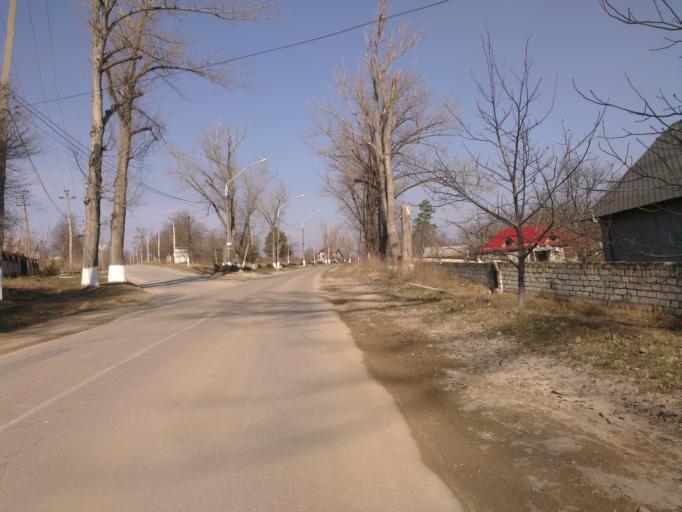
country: MD
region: Chisinau
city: Cricova
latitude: 47.1268
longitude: 28.8648
